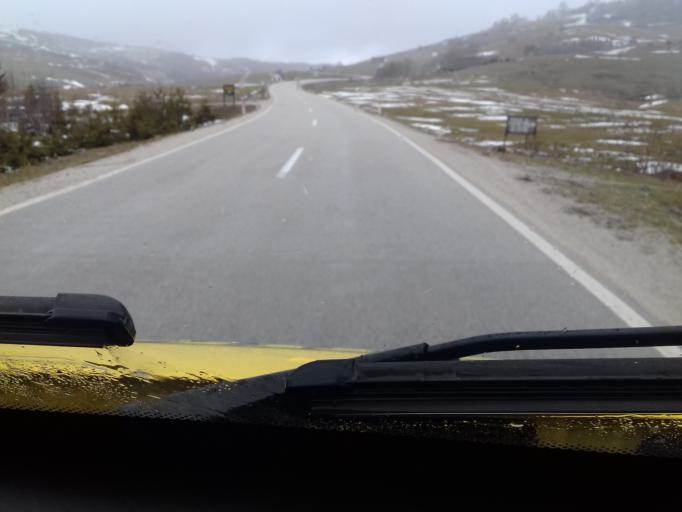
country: BA
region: Federation of Bosnia and Herzegovina
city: Novi Travnik
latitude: 44.1036
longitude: 17.5752
